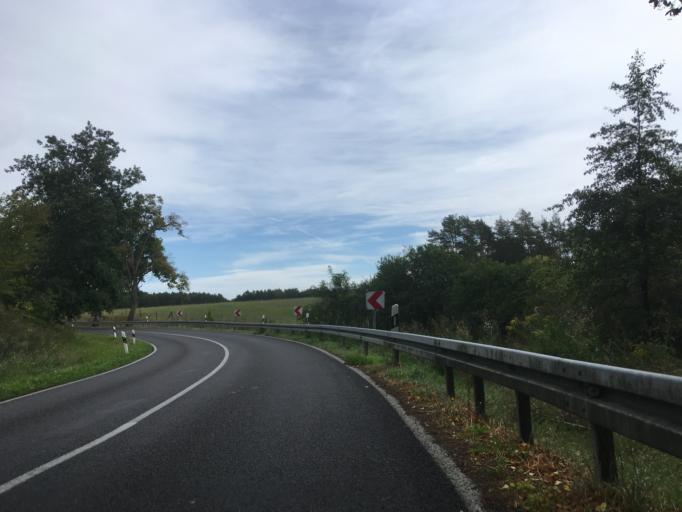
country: DE
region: Brandenburg
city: Templin
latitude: 53.1542
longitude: 13.5547
